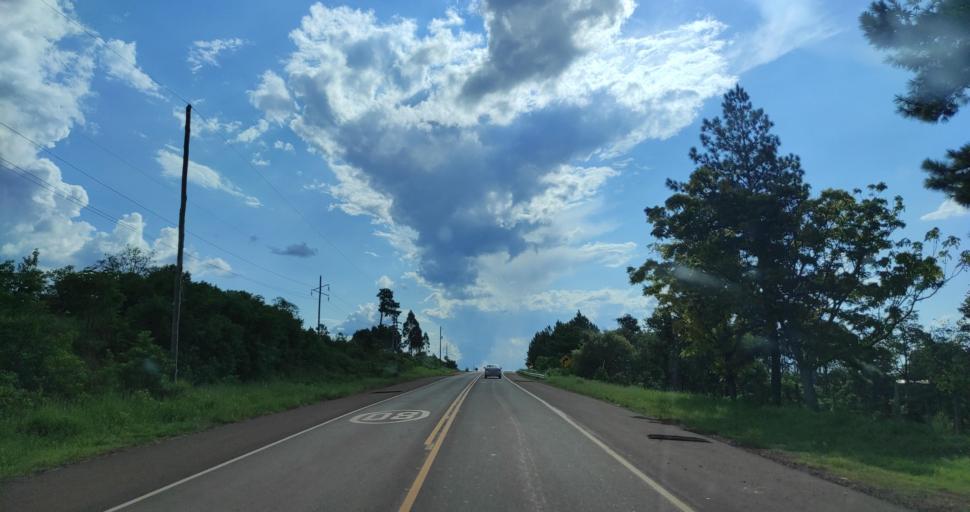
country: AR
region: Misiones
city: Bernardo de Irigoyen
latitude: -26.2946
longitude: -53.7782
